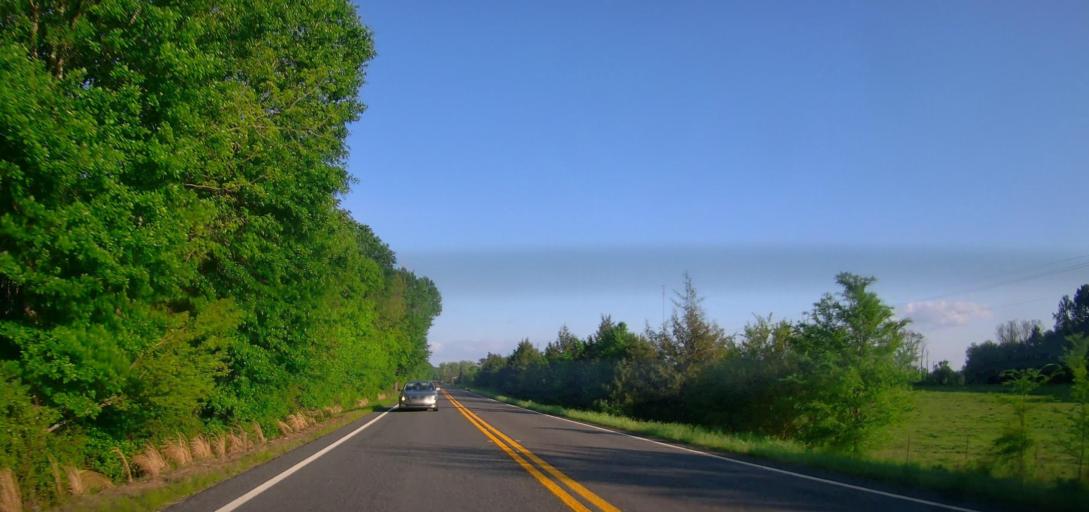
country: US
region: Georgia
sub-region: Jasper County
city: Monticello
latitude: 33.4482
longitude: -83.6272
